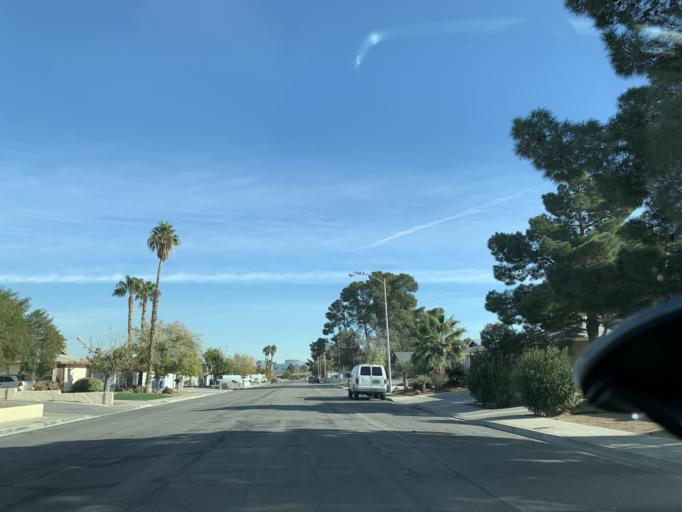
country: US
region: Nevada
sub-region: Clark County
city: Spring Valley
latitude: 36.1066
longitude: -115.2307
